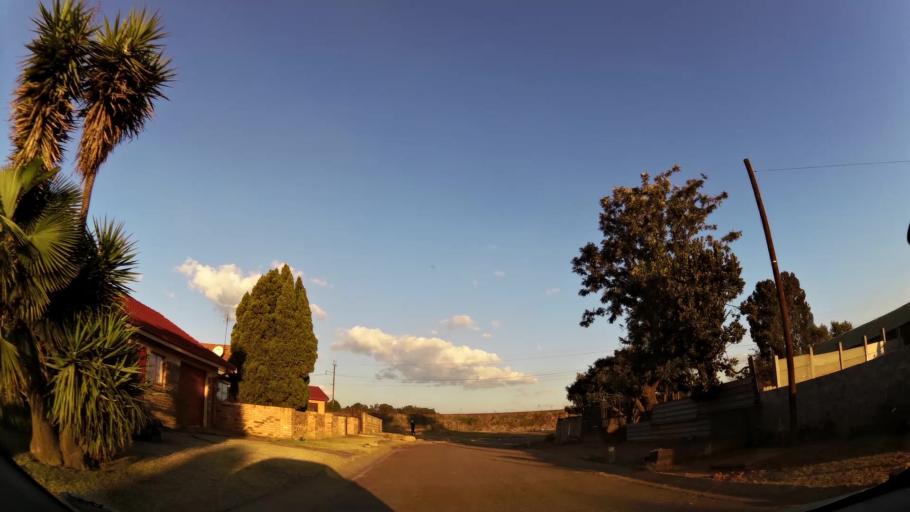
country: ZA
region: Mpumalanga
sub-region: Nkangala District Municipality
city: Witbank
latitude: -25.8876
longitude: 29.1822
